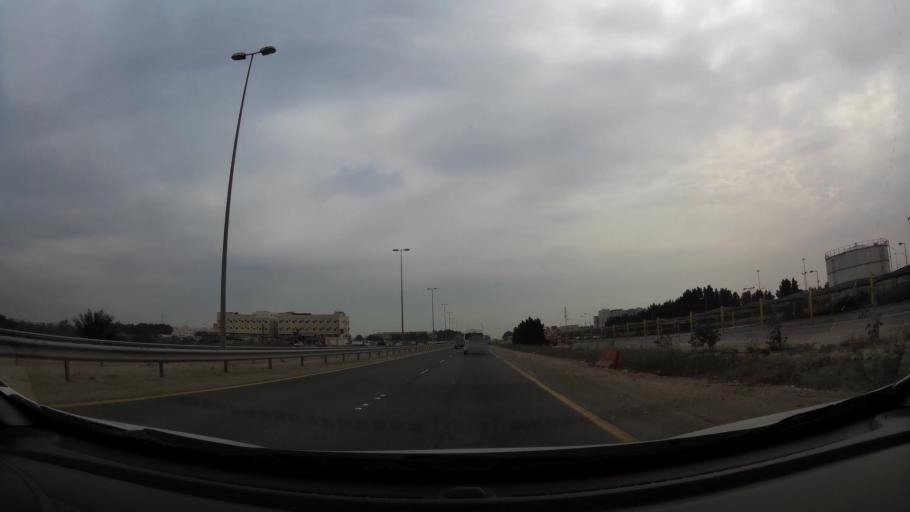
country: BH
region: Northern
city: Sitrah
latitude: 26.0877
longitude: 50.6109
